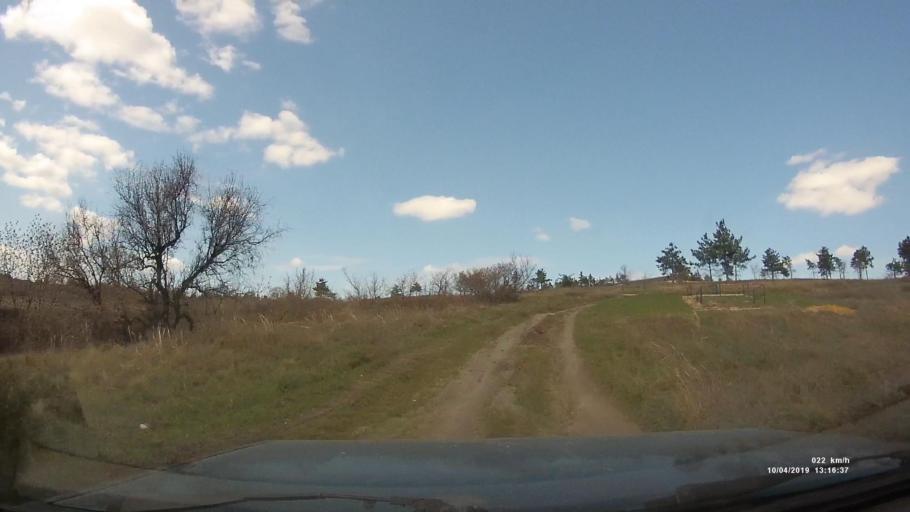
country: RU
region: Rostov
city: Masalovka
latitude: 48.4212
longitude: 40.2555
